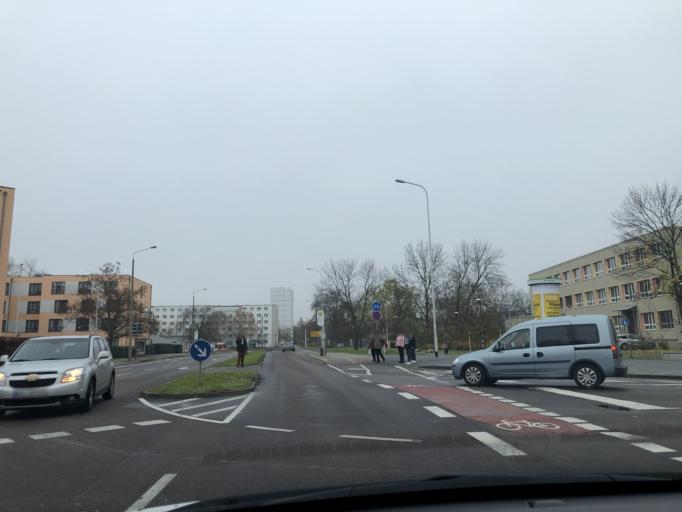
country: DE
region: Saxony-Anhalt
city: Halle Neustadt
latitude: 51.4820
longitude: 11.9286
